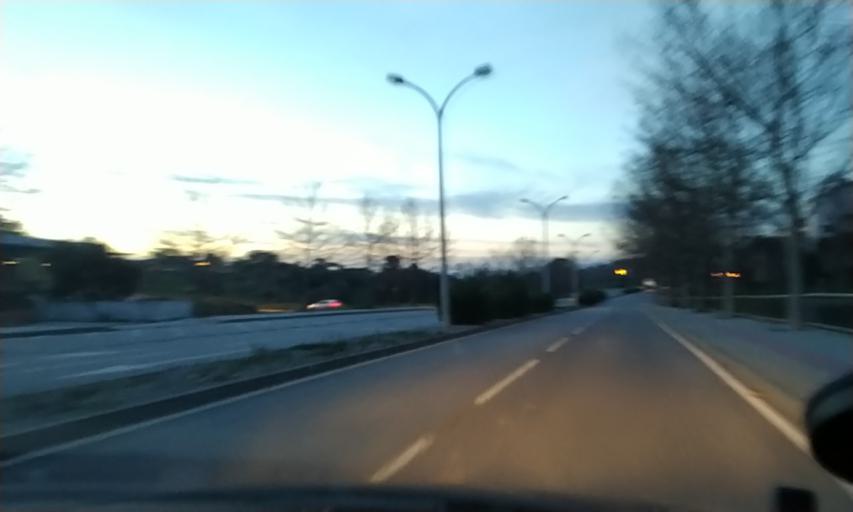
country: PT
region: Castelo Branco
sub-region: Castelo Branco
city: Castelo Branco
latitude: 39.8219
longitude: -7.5082
